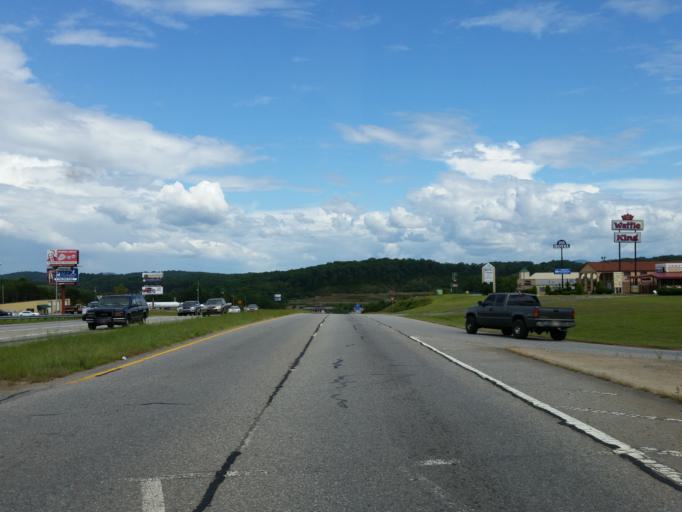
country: US
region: Georgia
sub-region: Fannin County
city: Blue Ridge
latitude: 34.8751
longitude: -84.3099
